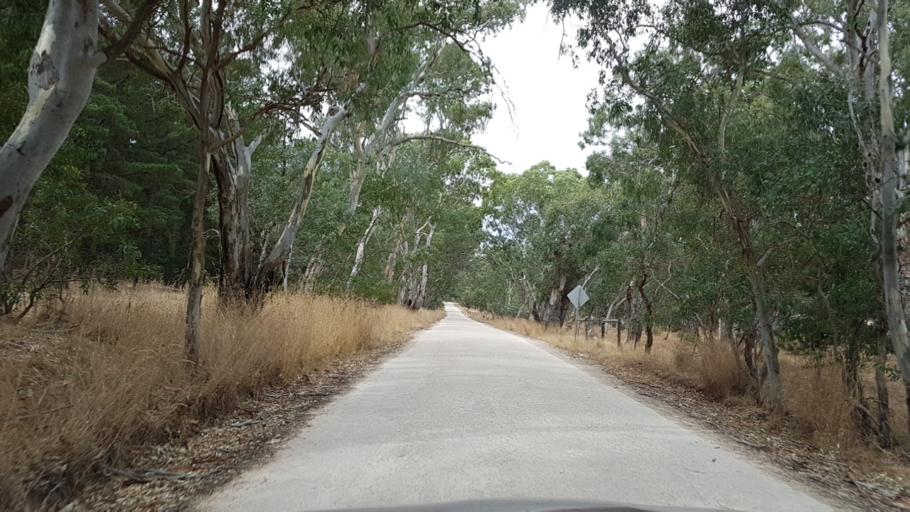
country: AU
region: South Australia
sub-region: Adelaide Hills
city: Birdwood
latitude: -34.7850
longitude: 138.9832
